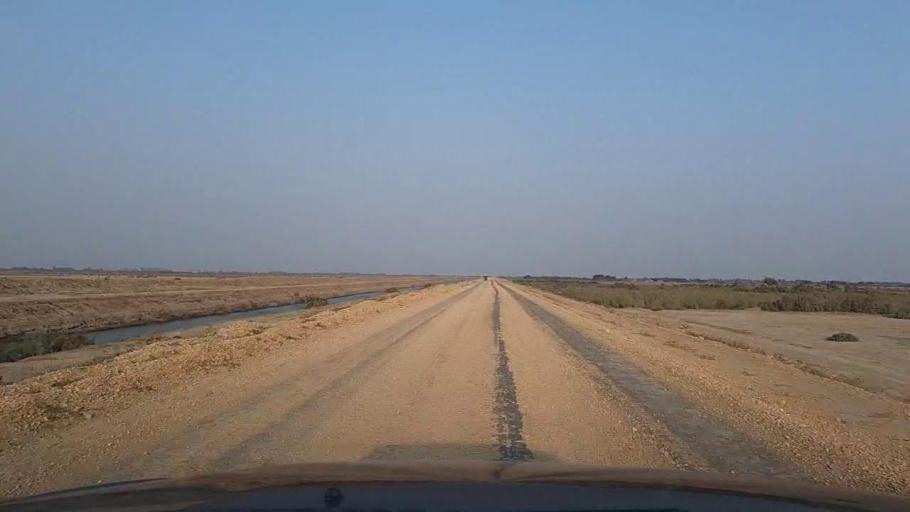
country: PK
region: Sindh
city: Mirpur Sakro
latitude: 24.4349
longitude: 67.7661
